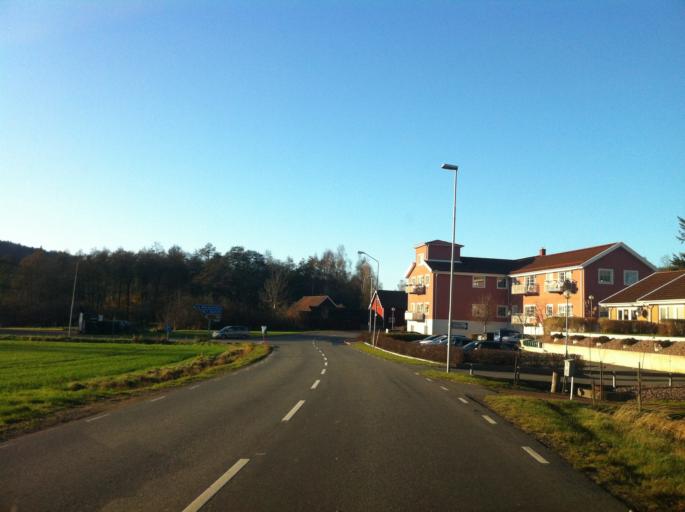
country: SE
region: Skane
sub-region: Bromolla Kommun
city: Nasum
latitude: 56.1600
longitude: 14.4406
